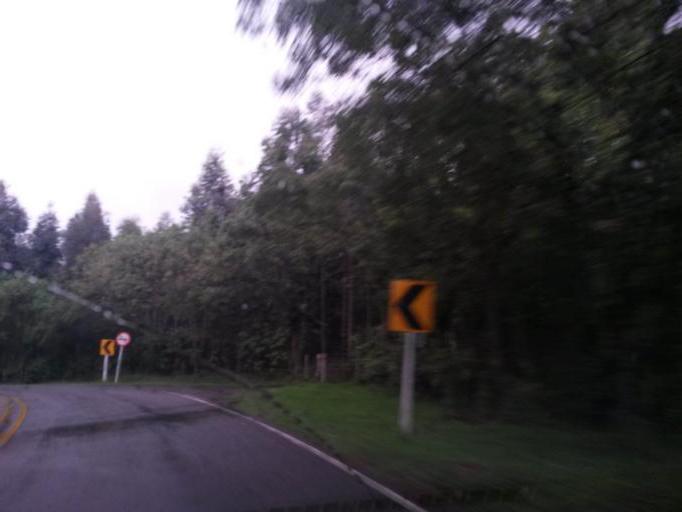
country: CO
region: Cauca
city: Popayan
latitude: 2.4073
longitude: -76.5086
